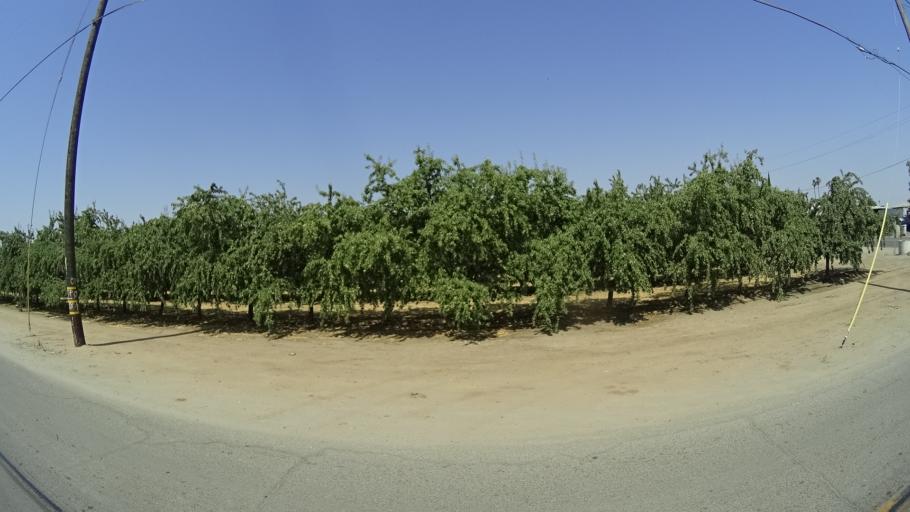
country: US
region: California
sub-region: Fresno County
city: West Park
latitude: 36.7352
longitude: -119.8534
